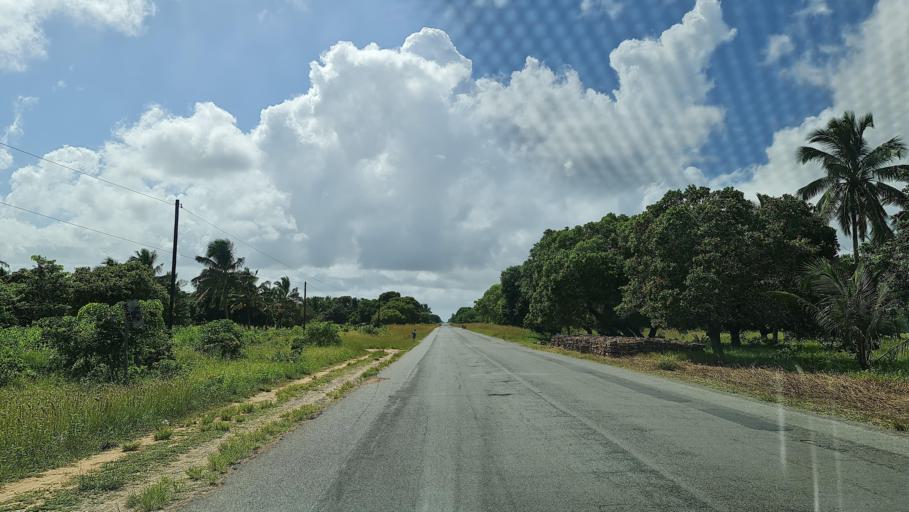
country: MZ
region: Gaza
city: Manjacaze
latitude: -24.6772
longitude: 34.5908
